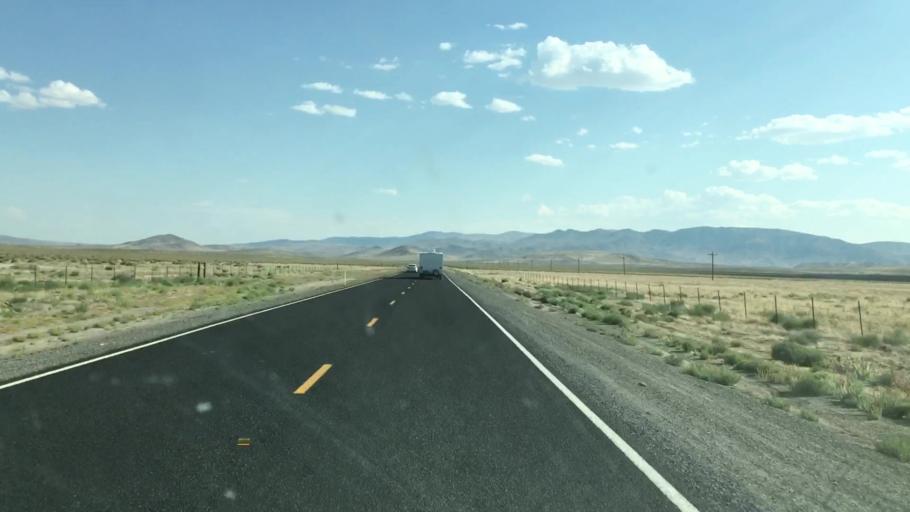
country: US
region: Nevada
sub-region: Lyon County
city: Fernley
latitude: 39.6793
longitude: -119.3339
